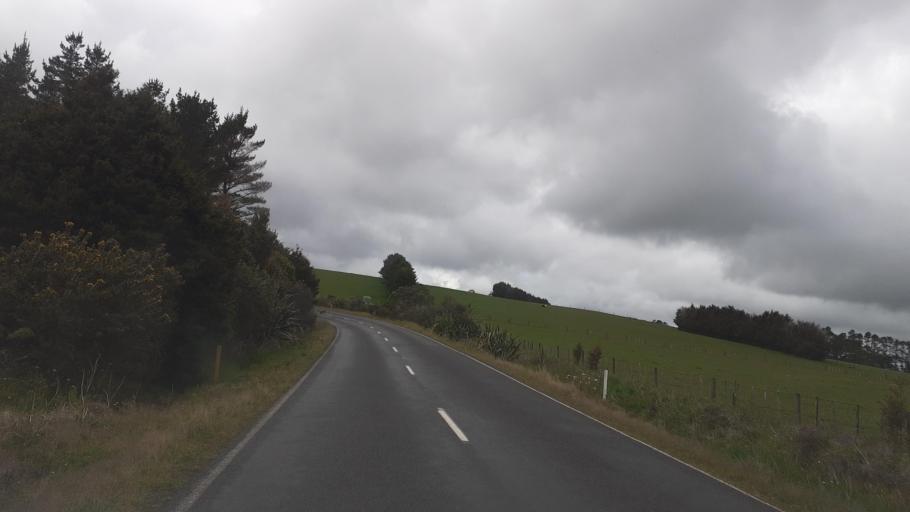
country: NZ
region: Northland
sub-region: Far North District
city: Waimate North
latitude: -35.2633
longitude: 173.8114
